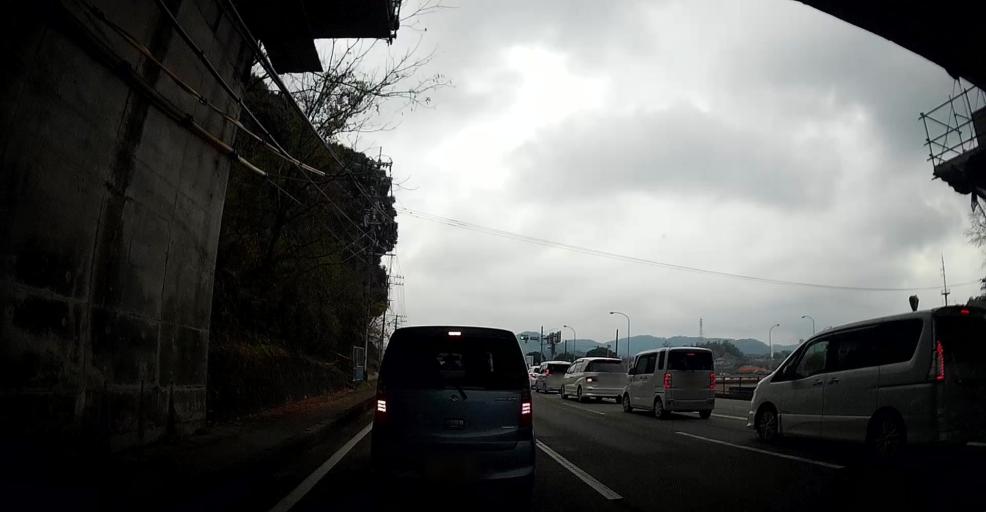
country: JP
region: Kumamoto
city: Matsubase
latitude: 32.6503
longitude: 130.7098
